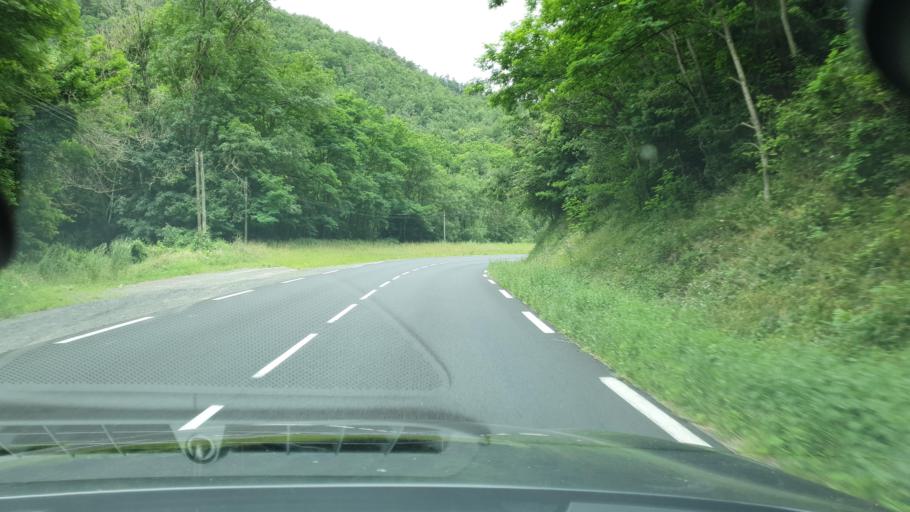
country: FR
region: Auvergne
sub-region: Departement du Puy-de-Dome
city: Champeix
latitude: 45.5785
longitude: 3.0727
